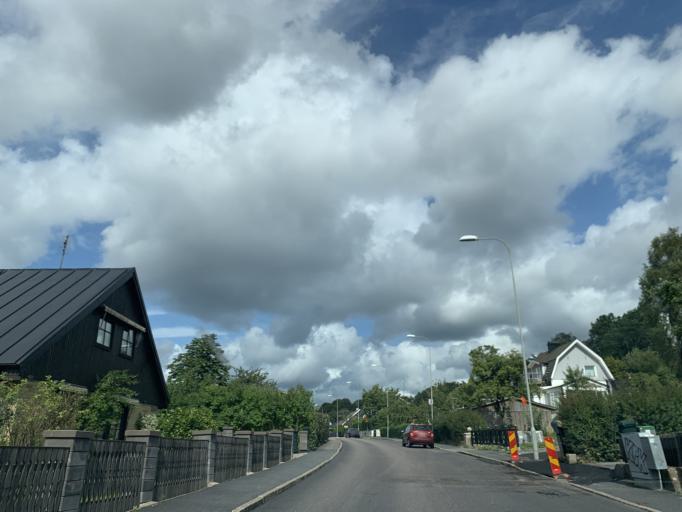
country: SE
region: Vaestra Goetaland
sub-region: Goteborg
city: Eriksbo
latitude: 57.7532
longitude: 12.0490
